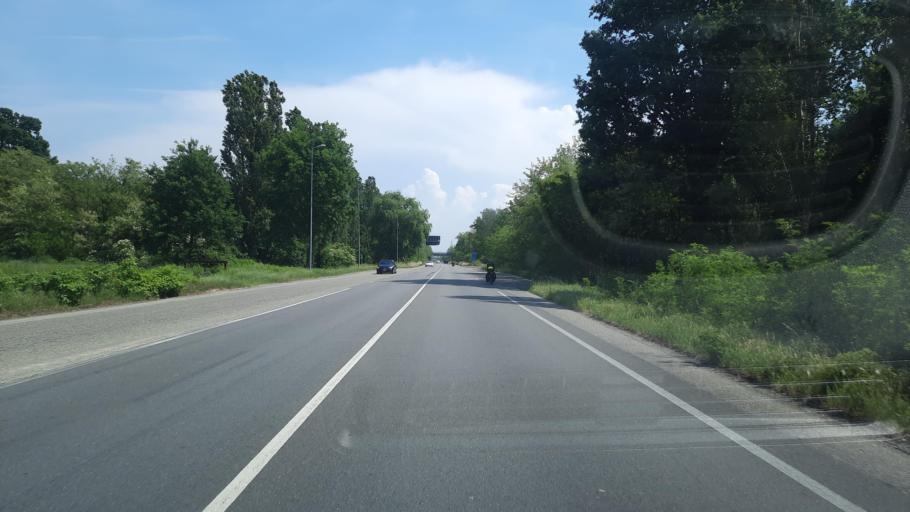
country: IT
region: Lombardy
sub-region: Provincia di Pavia
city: Gropello Cairoli
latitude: 45.1788
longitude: 8.9680
